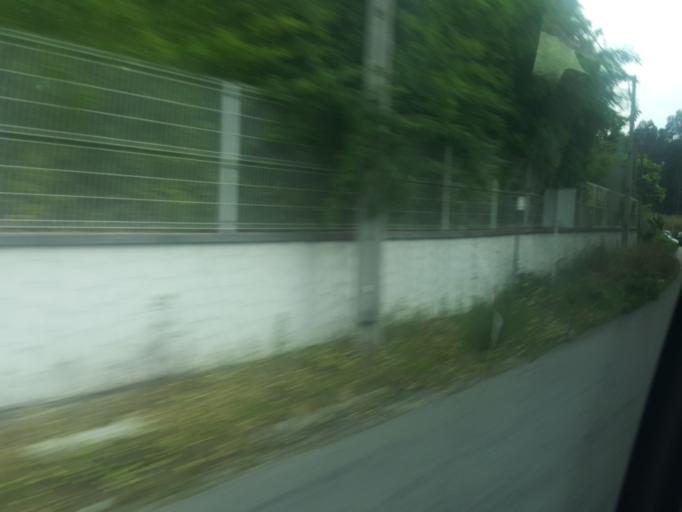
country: PT
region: Porto
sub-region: Marco de Canaveses
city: Marco de Canavezes
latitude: 41.1990
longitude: -8.1790
